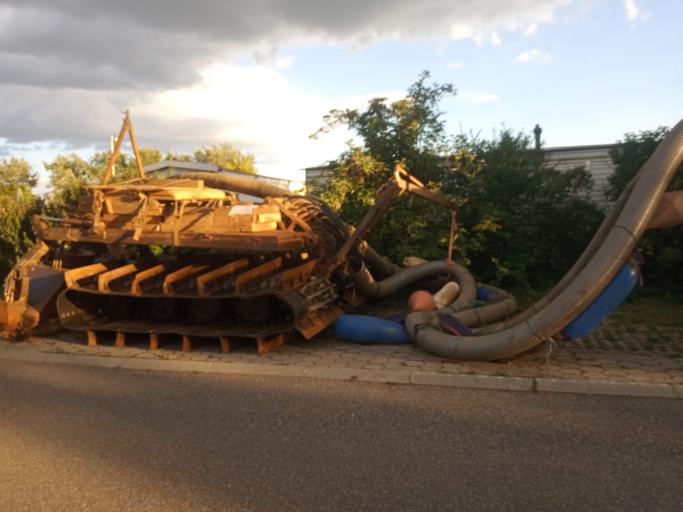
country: AT
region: Burgenland
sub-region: Rust Stadt
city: Rust
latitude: 47.8010
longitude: 16.6945
